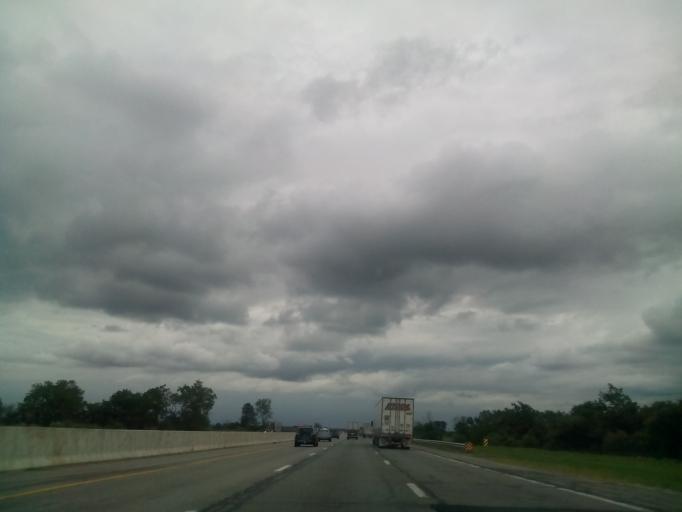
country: US
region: Ohio
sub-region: Wood County
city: Walbridge
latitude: 41.5475
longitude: -83.5365
